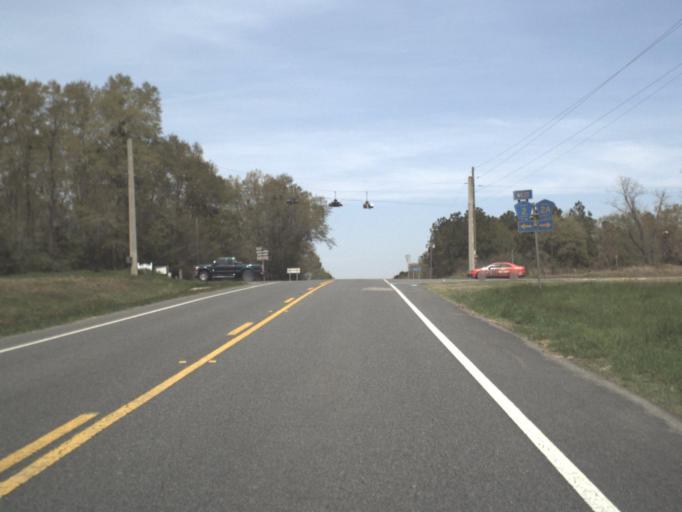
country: US
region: Alabama
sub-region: Geneva County
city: Samson
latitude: 30.9753
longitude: -85.9978
